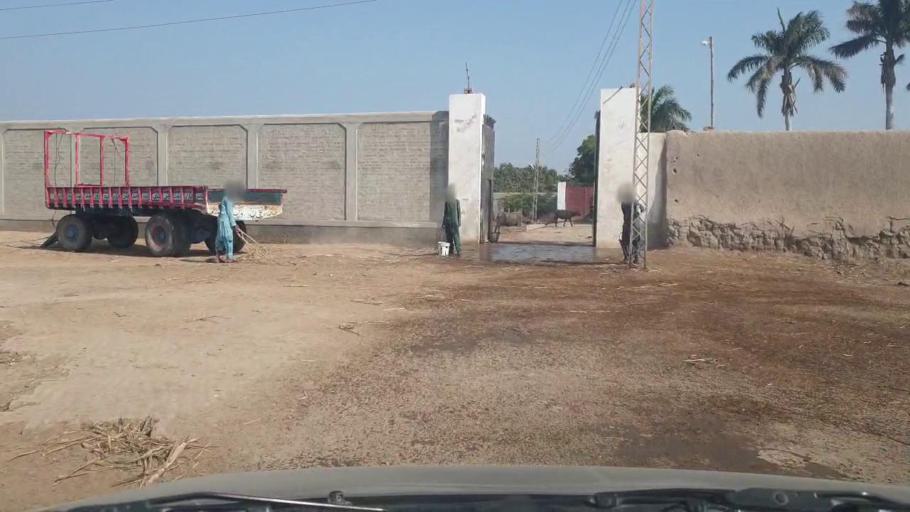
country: PK
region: Sindh
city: Mirwah Gorchani
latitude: 25.2594
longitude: 69.0920
